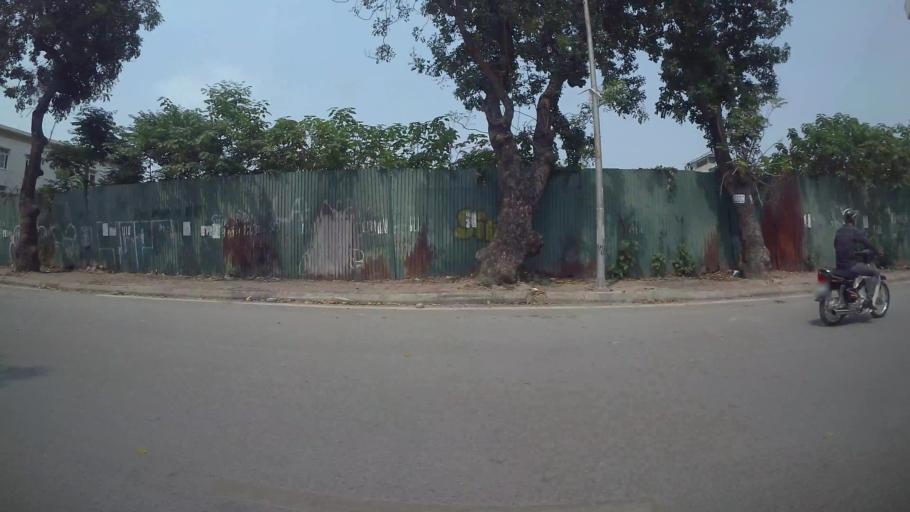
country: VN
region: Ha Noi
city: Hai BaTrung
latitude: 21.0096
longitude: 105.8374
